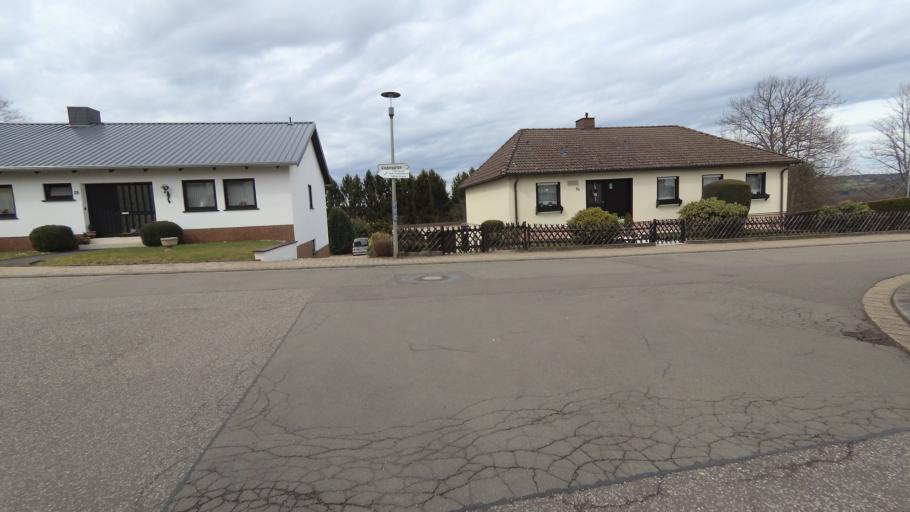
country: DE
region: Saarland
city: Friedrichsthal
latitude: 49.3578
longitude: 7.1032
